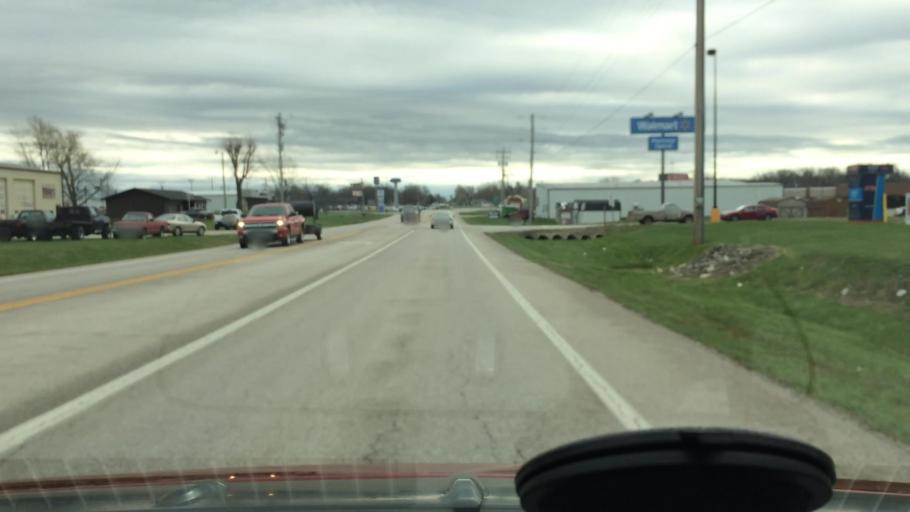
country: US
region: Missouri
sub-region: Webster County
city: Marshfield
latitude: 37.3401
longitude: -92.9395
